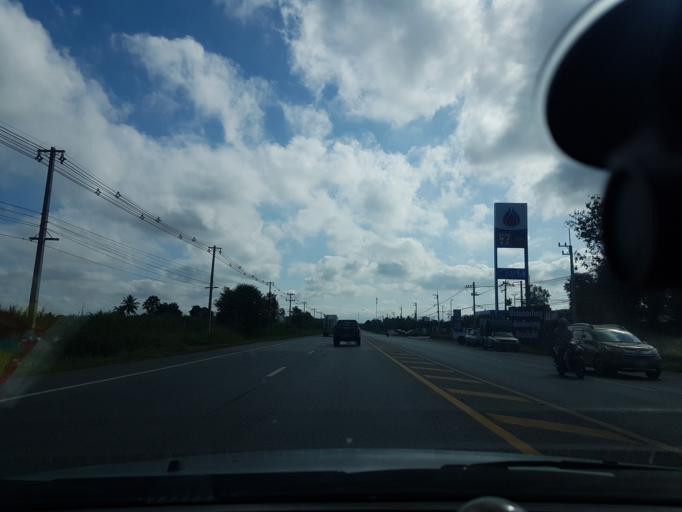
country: TH
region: Lop Buri
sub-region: Amphoe Tha Luang
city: Tha Luang
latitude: 15.0793
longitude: 101.0320
